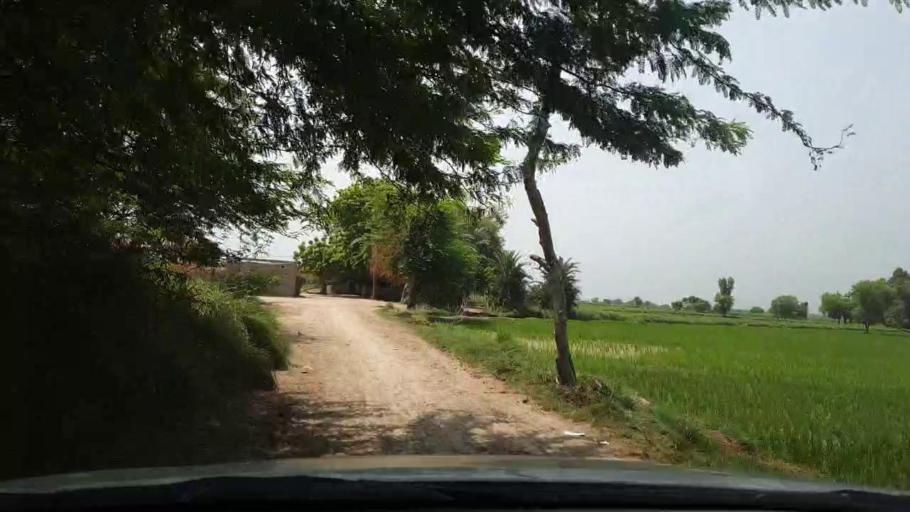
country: PK
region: Sindh
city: Rustam jo Goth
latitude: 27.9757
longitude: 68.7217
